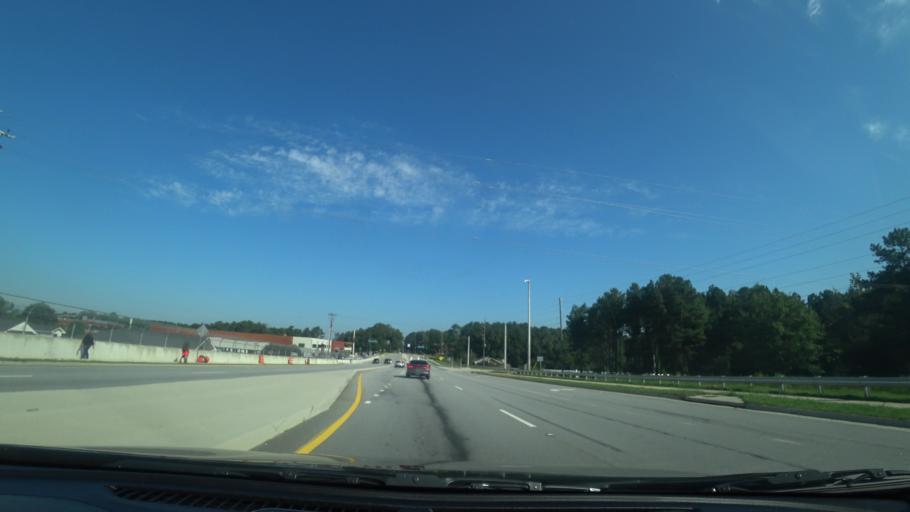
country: US
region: Georgia
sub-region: Gwinnett County
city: Lawrenceville
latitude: 33.9785
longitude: -83.9968
